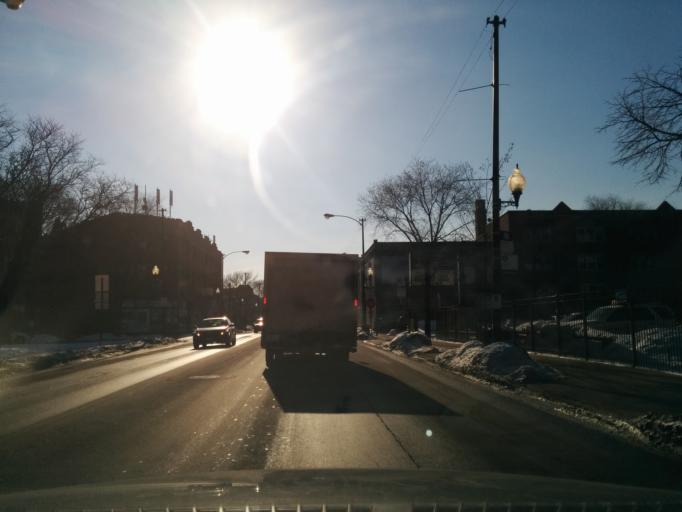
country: US
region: Illinois
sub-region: Cook County
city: Lincolnwood
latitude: 41.9382
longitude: -87.7224
